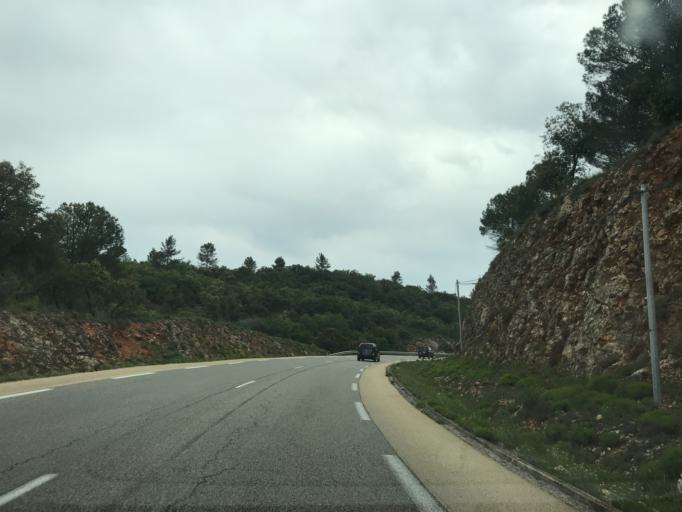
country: FR
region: Provence-Alpes-Cote d'Azur
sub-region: Departement du Var
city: Rians
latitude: 43.5894
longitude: 5.7482
